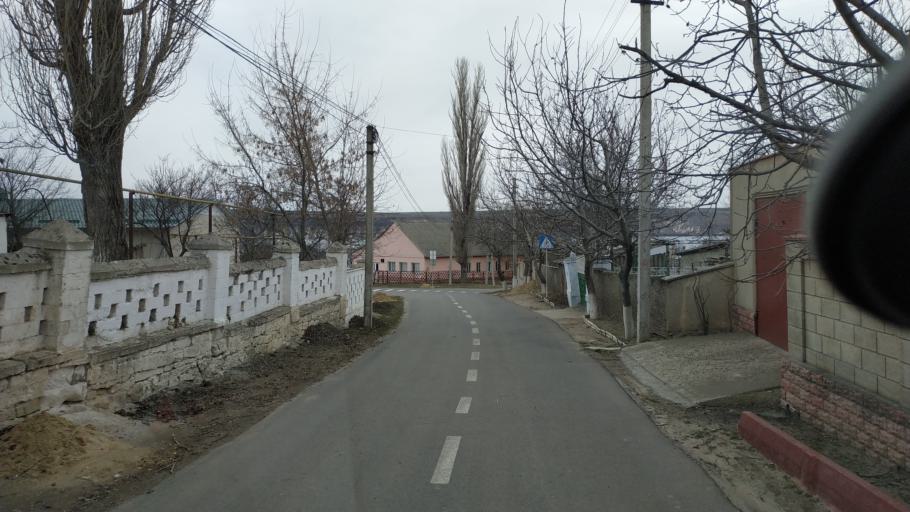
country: MD
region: Telenesti
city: Cocieri
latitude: 47.3477
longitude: 29.0910
